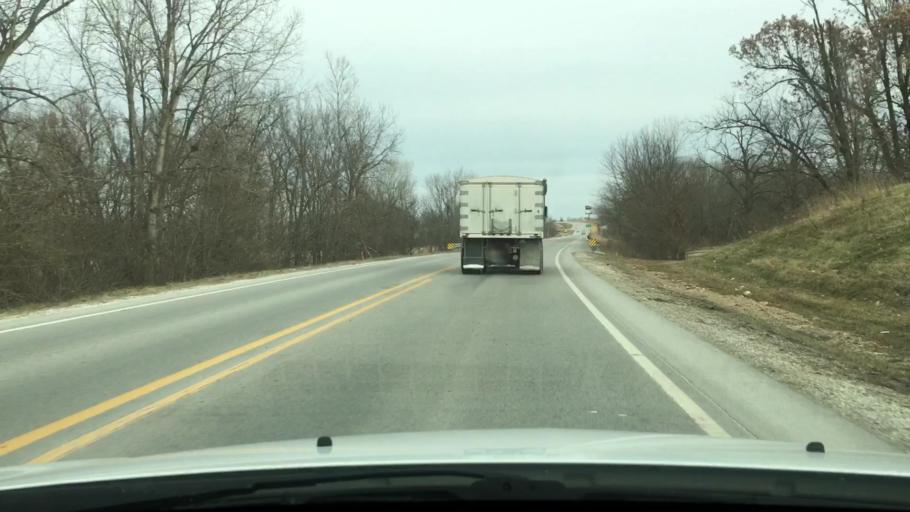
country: US
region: Illinois
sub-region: Pike County
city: Pittsfield
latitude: 39.6248
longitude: -90.7983
